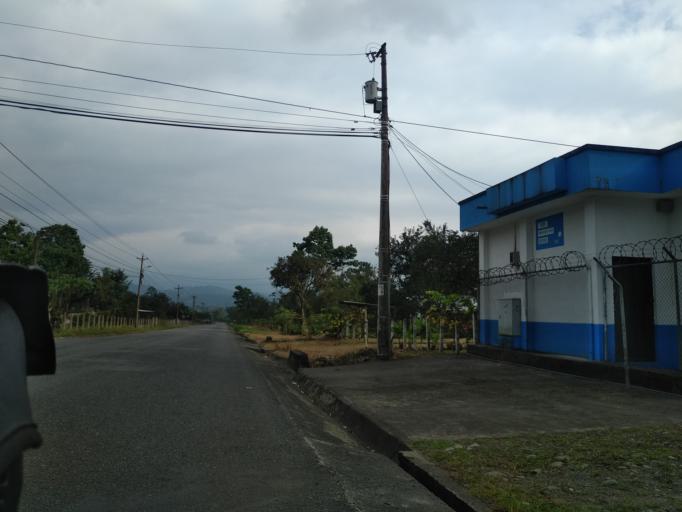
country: EC
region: Cotopaxi
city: La Mana
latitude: -0.8980
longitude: -79.1620
